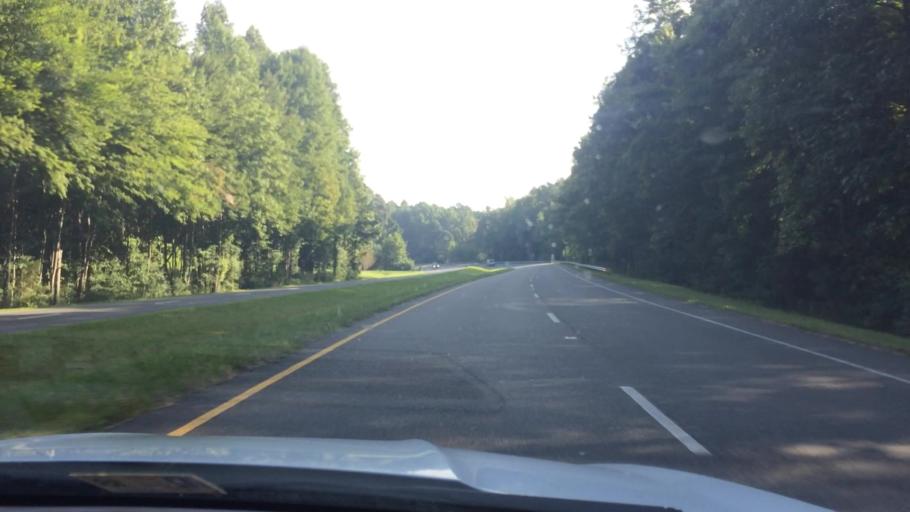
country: US
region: Virginia
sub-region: Gloucester County
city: Gloucester Courthouse
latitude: 37.4523
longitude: -76.4709
